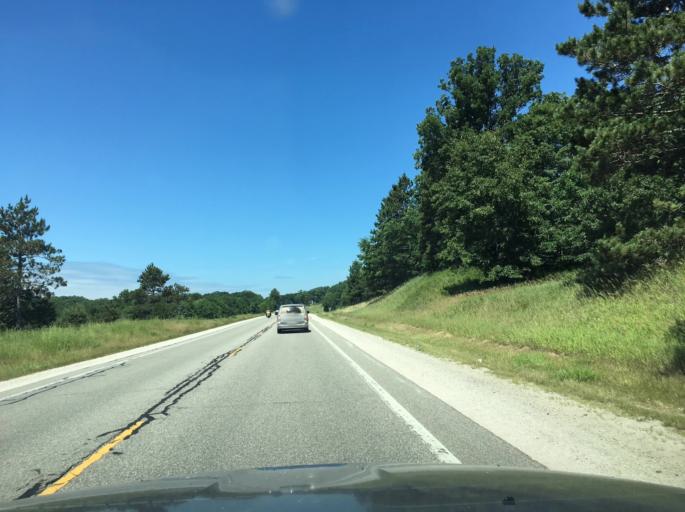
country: US
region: Michigan
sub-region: Osceola County
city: Reed City
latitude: 43.8895
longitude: -85.6465
